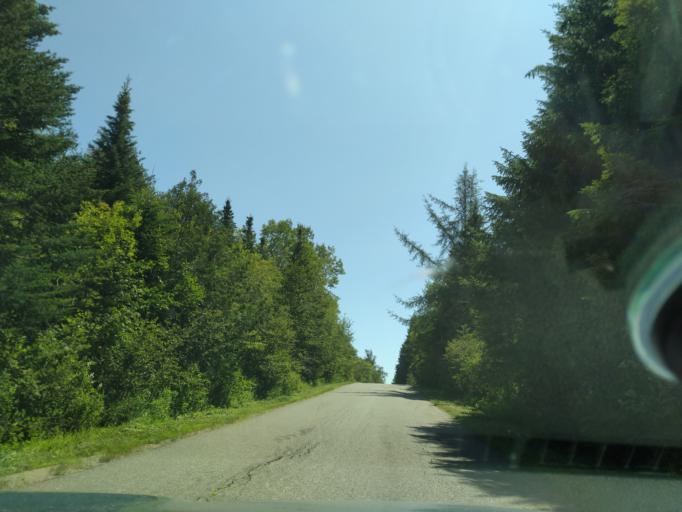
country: US
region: Maine
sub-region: Washington County
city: Eastport
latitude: 44.8343
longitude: -67.0091
